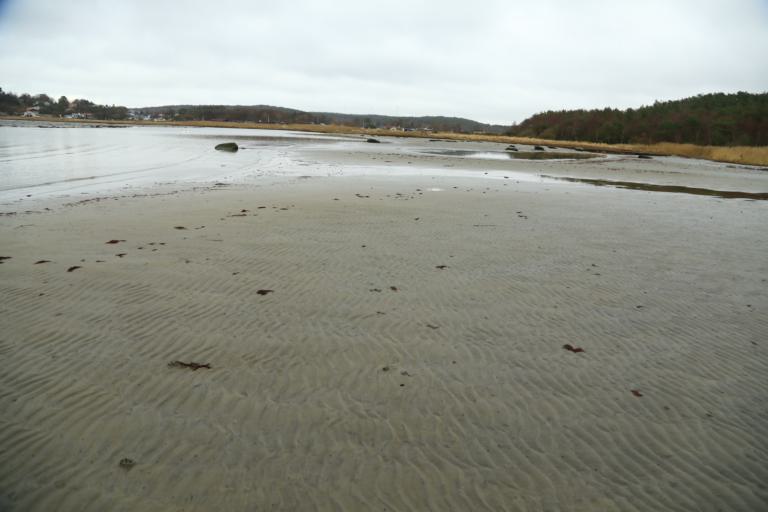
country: SE
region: Halland
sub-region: Varbergs Kommun
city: Varberg
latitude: 57.1792
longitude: 12.2101
